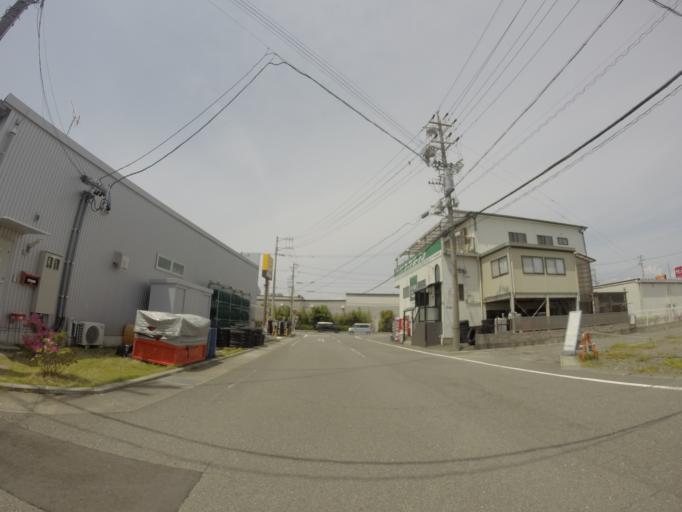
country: JP
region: Shizuoka
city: Yaizu
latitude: 34.8453
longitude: 138.3185
